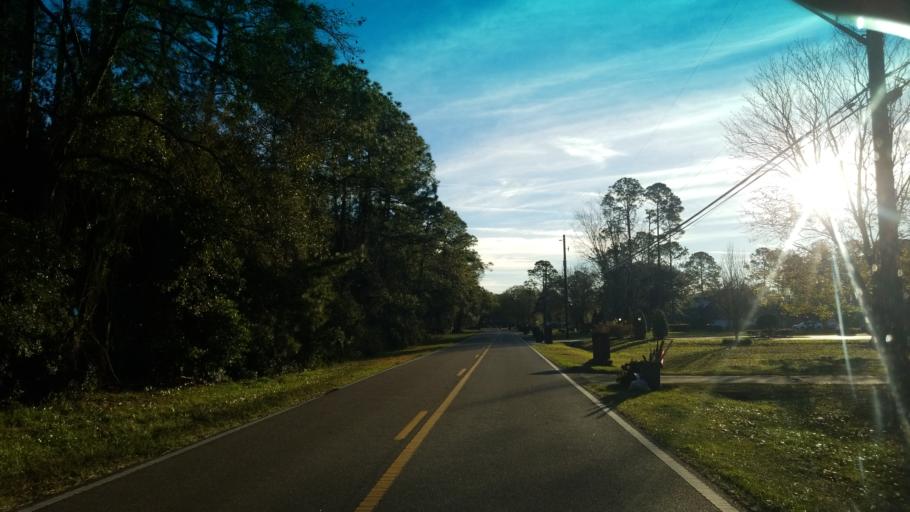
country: US
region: Florida
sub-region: Duval County
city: Jacksonville
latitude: 30.3454
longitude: -81.7930
